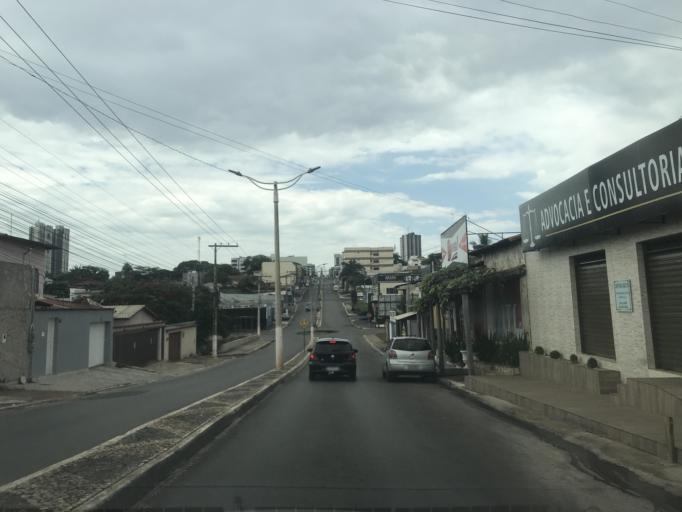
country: BR
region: Goias
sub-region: Luziania
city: Luziania
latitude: -16.2481
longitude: -47.9515
